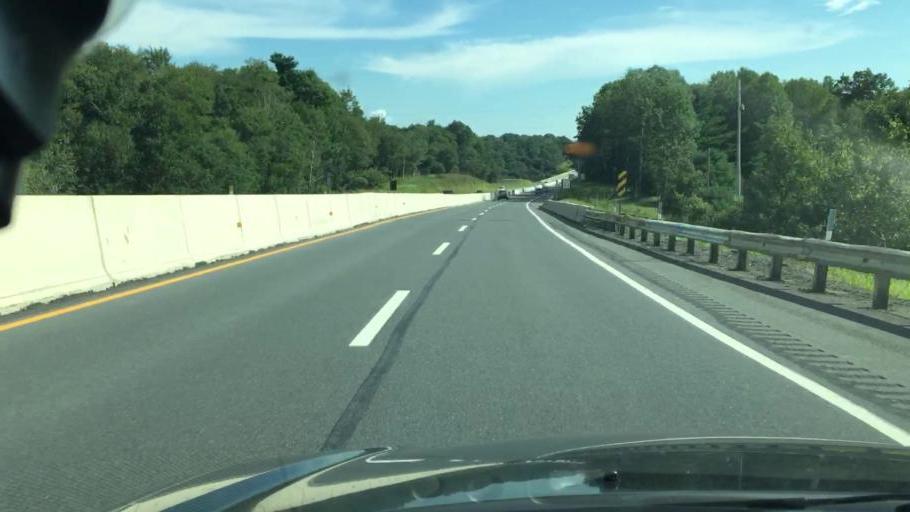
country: US
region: Pennsylvania
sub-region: Carbon County
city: Towamensing Trails
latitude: 41.0099
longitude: -75.6368
